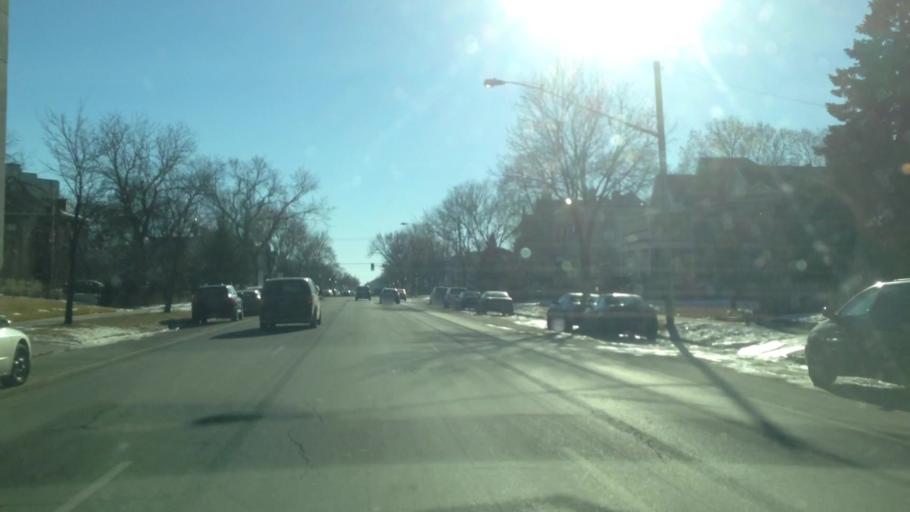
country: US
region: Minnesota
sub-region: Hennepin County
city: Minneapolis
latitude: 44.9570
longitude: -93.2677
